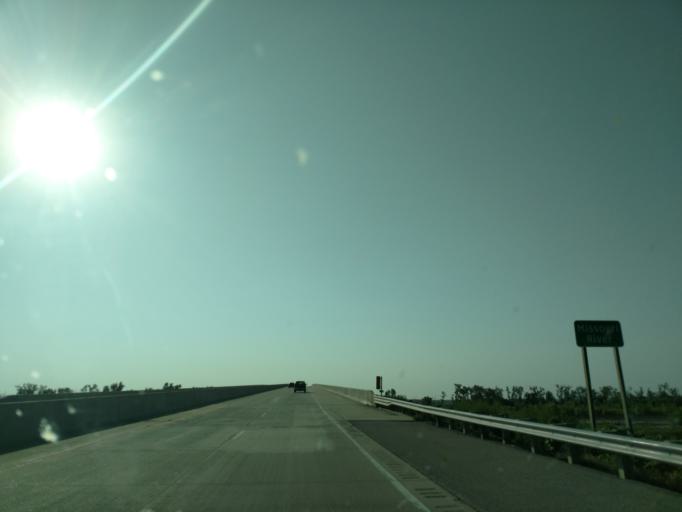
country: US
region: Nebraska
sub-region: Cass County
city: Plattsmouth
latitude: 41.0648
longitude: -95.8727
